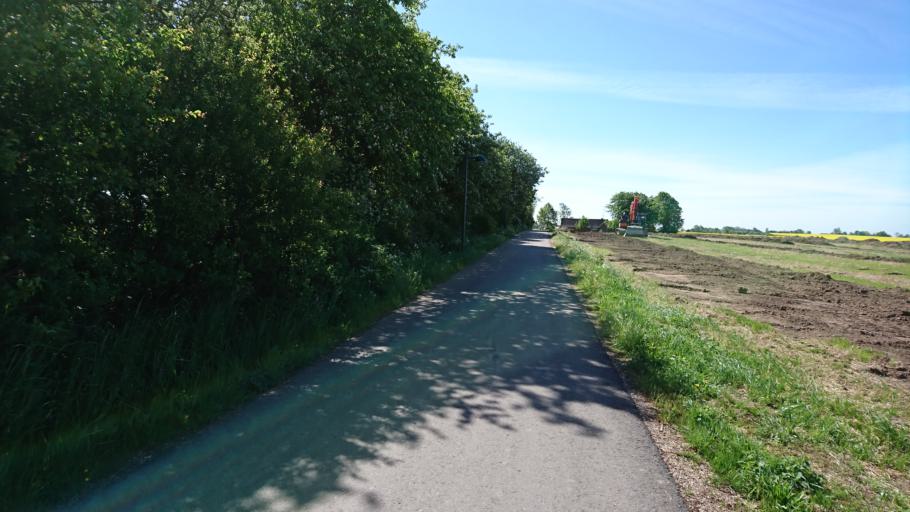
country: DK
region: Capital Region
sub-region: Egedal Kommune
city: Olstykke
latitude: 55.8087
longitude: 12.1145
